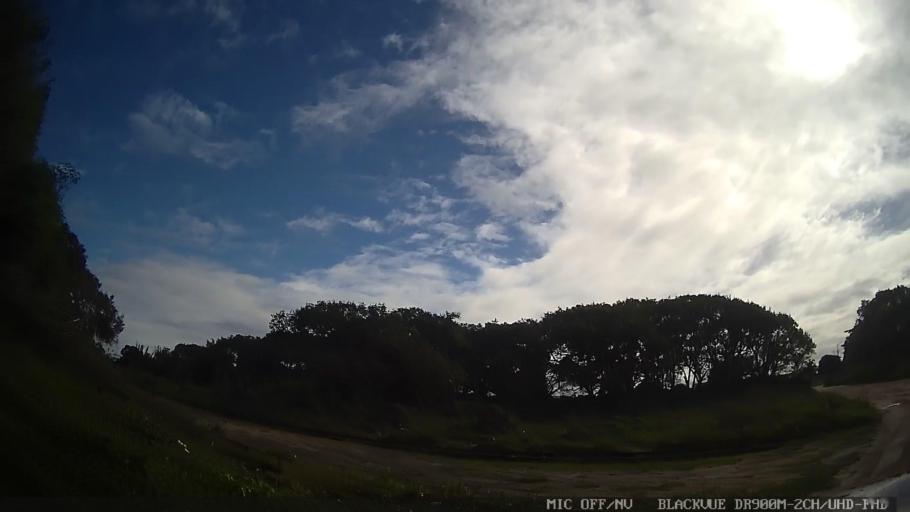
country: BR
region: Sao Paulo
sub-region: Itanhaem
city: Itanhaem
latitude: -24.2469
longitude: -46.8960
